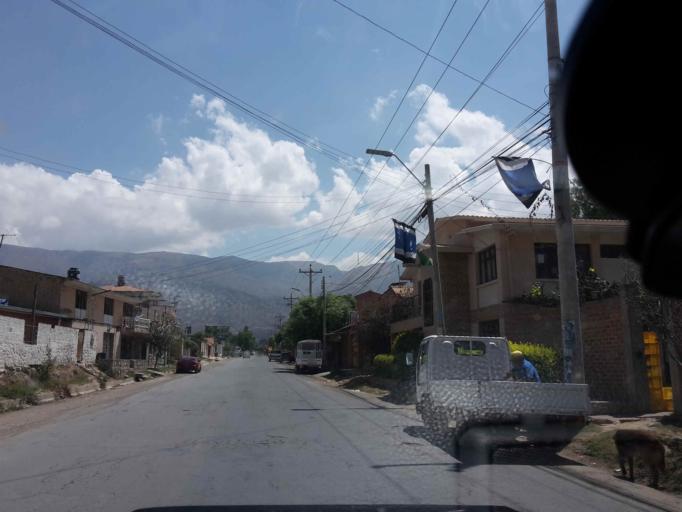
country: BO
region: Cochabamba
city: Cochabamba
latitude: -17.3594
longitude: -66.2283
